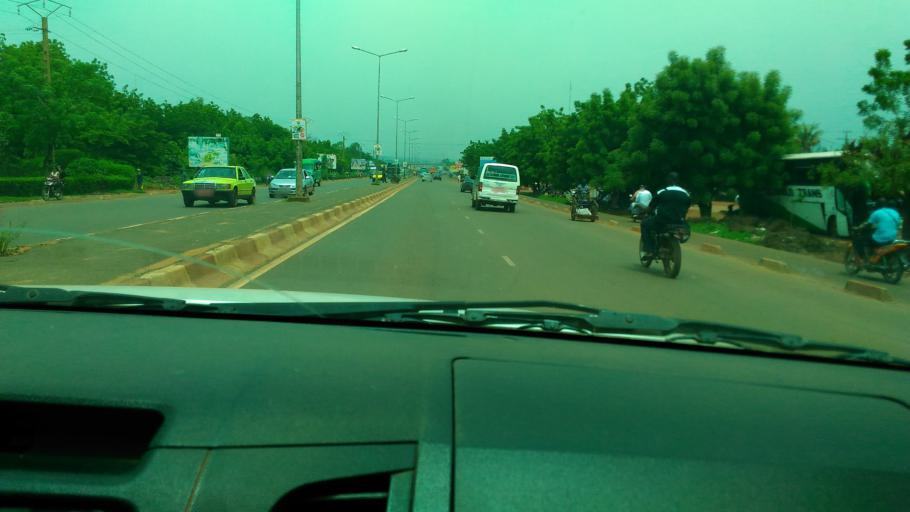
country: ML
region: Bamako
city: Bamako
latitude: 12.5946
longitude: -7.9564
